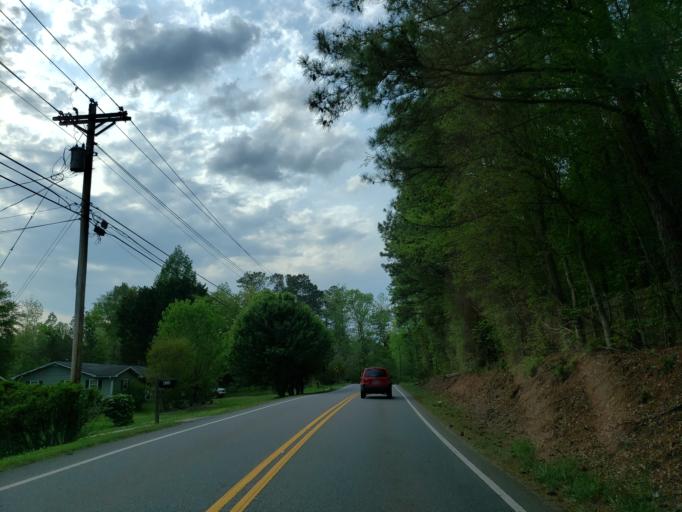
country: US
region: Georgia
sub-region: Cherokee County
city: Woodstock
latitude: 34.1201
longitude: -84.4905
